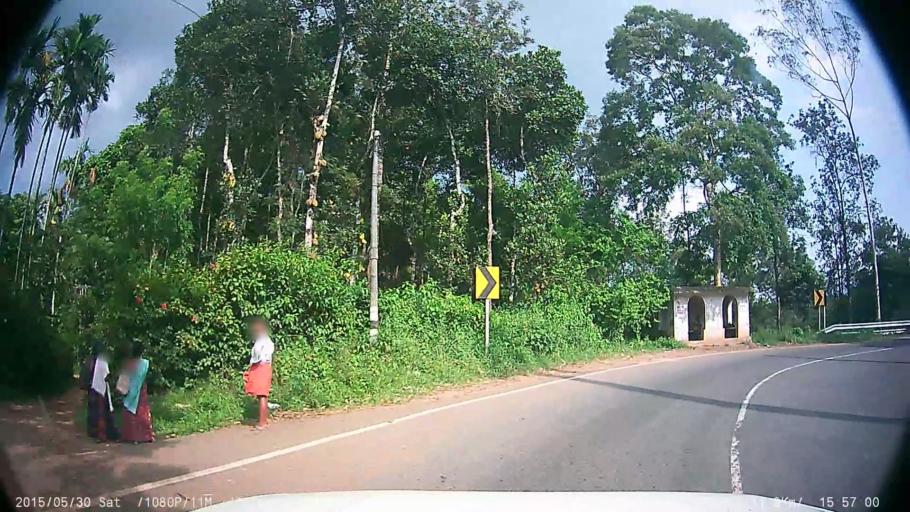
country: IN
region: Kerala
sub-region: Wayanad
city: Kalpetta
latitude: 11.6562
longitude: 76.0879
